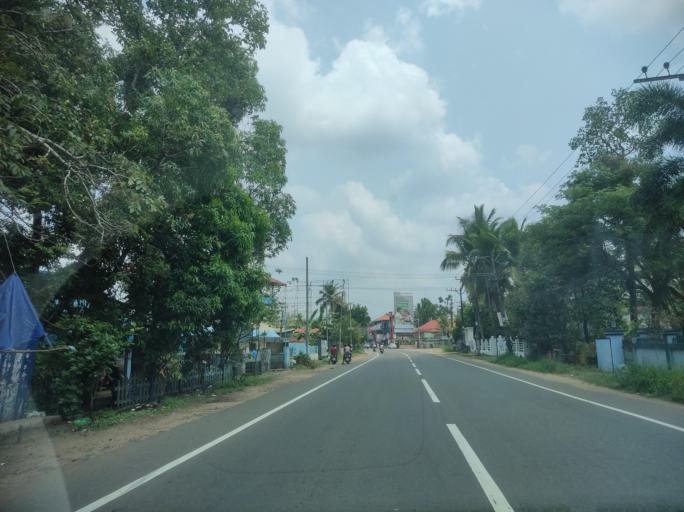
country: IN
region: Kerala
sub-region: Kottayam
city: Changanacheri
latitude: 9.4253
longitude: 76.5462
